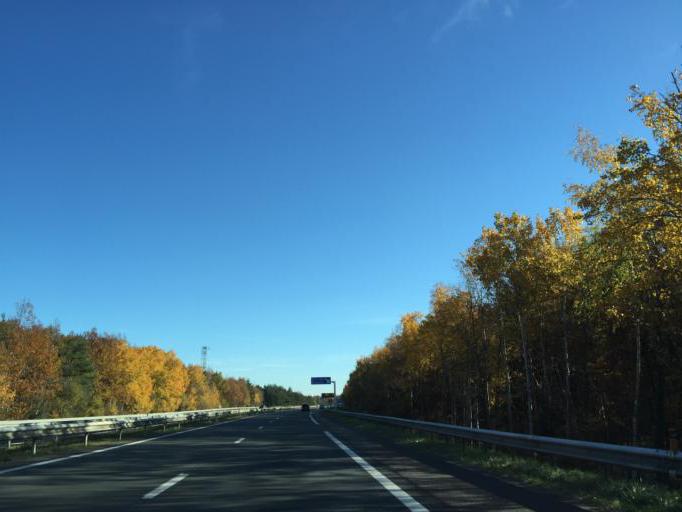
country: FR
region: Rhone-Alpes
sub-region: Departement de la Loire
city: Saint-Germain-Laval
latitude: 45.8433
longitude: 4.0879
